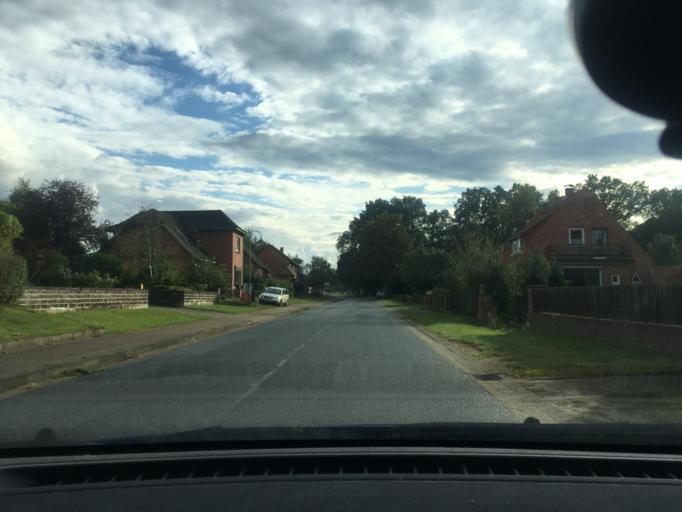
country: DE
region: Lower Saxony
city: Neu Darchau
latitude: 53.2242
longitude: 10.8829
